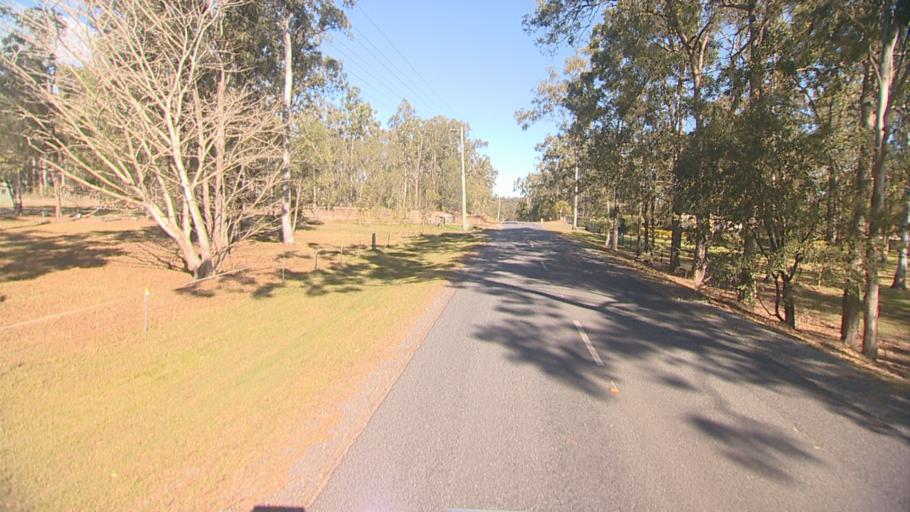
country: AU
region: Queensland
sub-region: Logan
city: Chambers Flat
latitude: -27.8104
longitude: 153.0719
